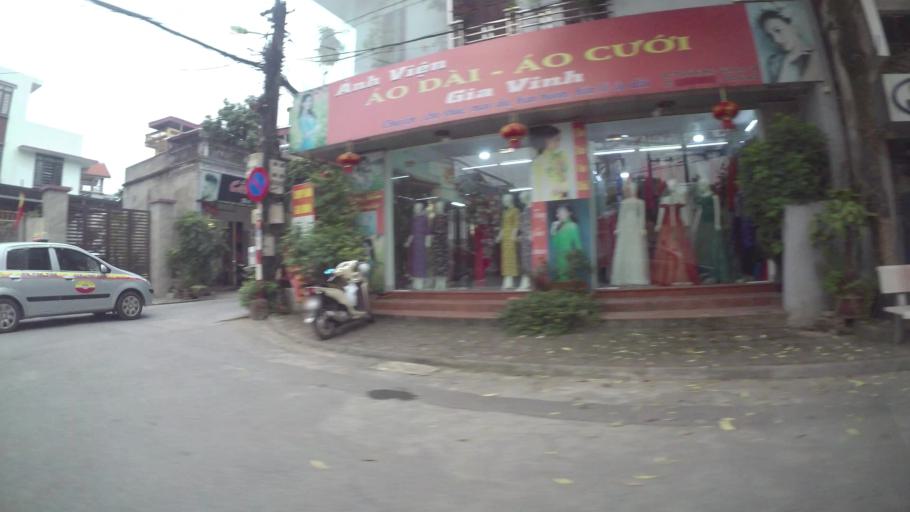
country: VN
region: Ha Noi
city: Trau Quy
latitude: 21.0571
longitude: 105.8989
